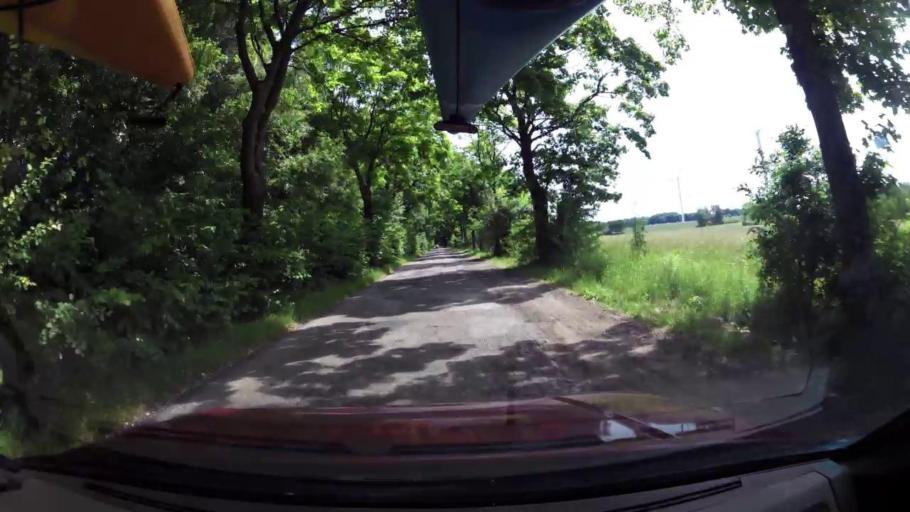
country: PL
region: West Pomeranian Voivodeship
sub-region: Powiat slawienski
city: Darlowo
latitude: 54.3261
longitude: 16.3616
